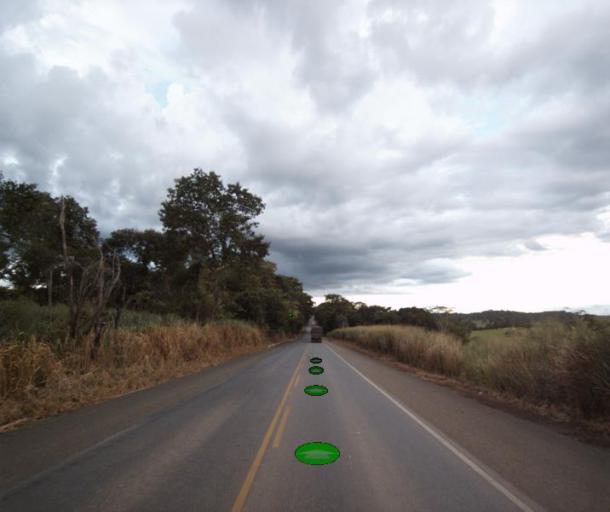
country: BR
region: Goias
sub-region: Uruacu
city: Uruacu
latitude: -14.7373
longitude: -49.2434
